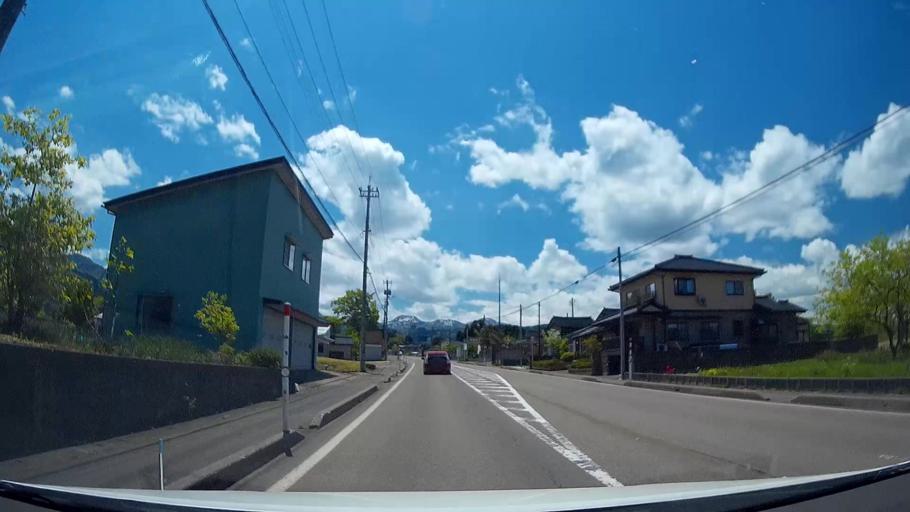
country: JP
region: Toyama
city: Fukumitsu
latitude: 36.5067
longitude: 136.8987
